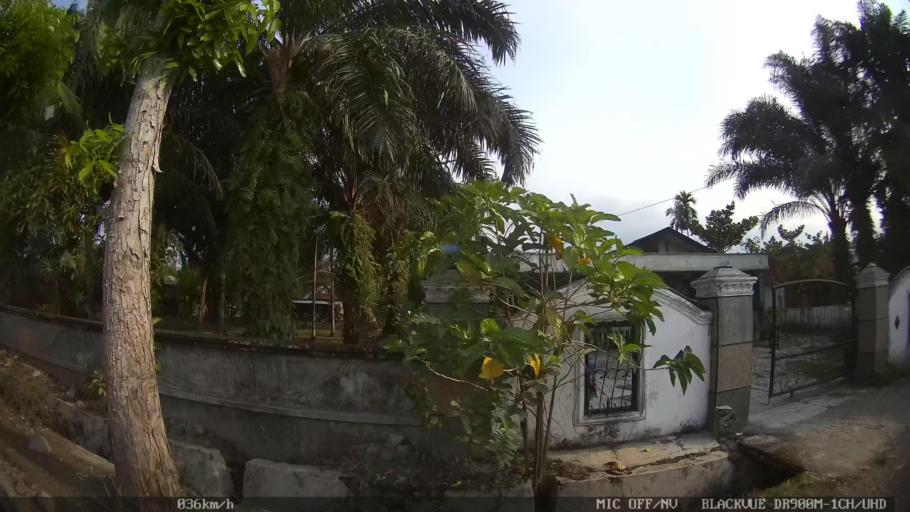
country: ID
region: North Sumatra
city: Binjai
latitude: 3.6173
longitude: 98.5290
